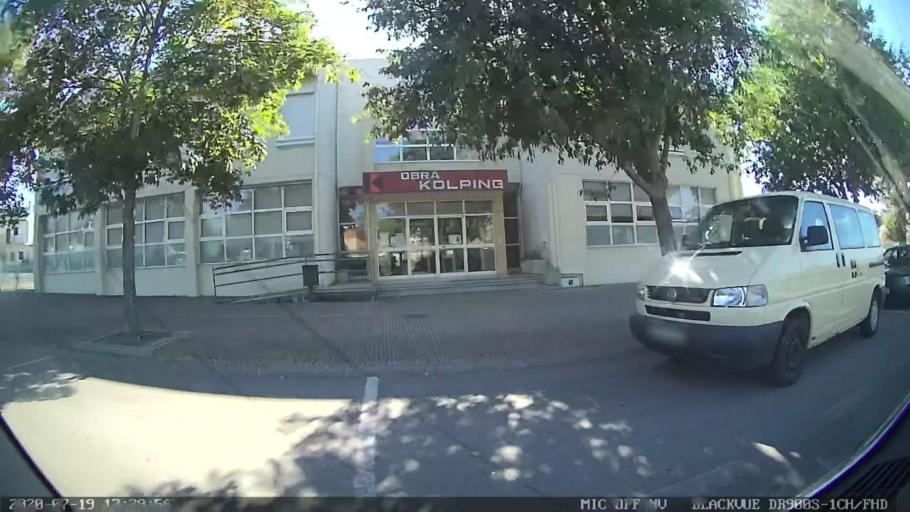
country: PT
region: Braganca
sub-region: Braganca Municipality
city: Braganca
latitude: 41.7961
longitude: -6.7710
